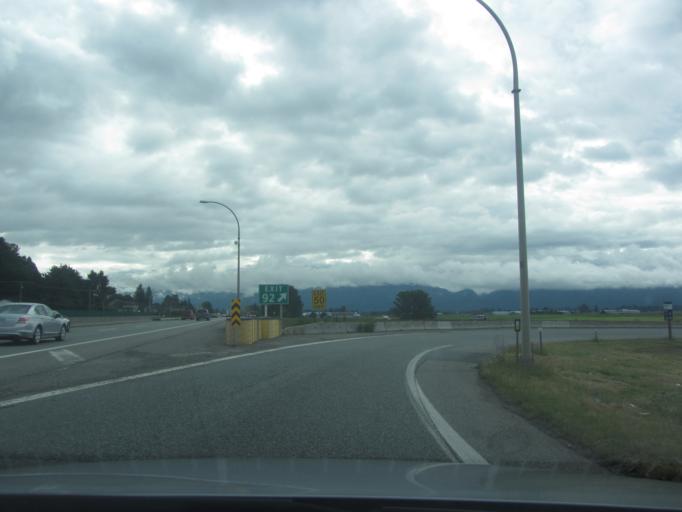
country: CA
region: British Columbia
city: Abbotsford
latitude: 49.0333
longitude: -122.2642
